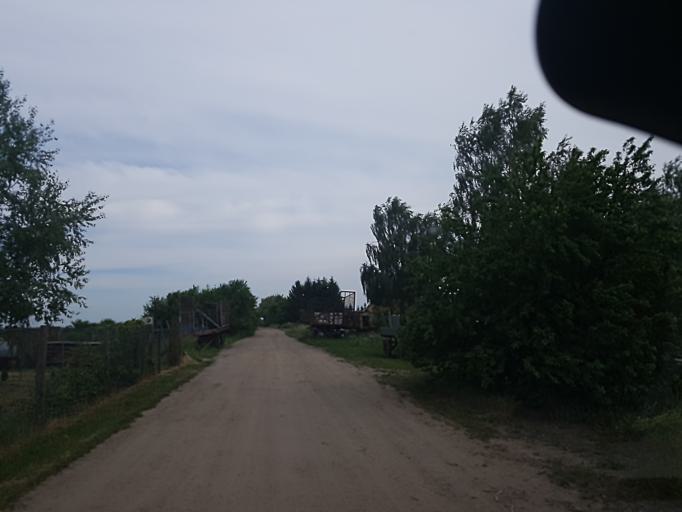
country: DE
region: Brandenburg
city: Gorzke
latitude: 52.1071
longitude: 12.3741
